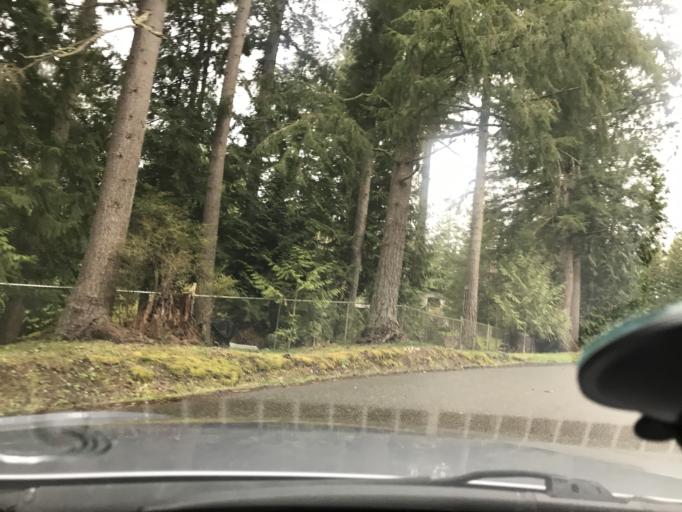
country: US
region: Washington
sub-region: King County
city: Ames Lake
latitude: 47.6431
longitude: -121.9610
